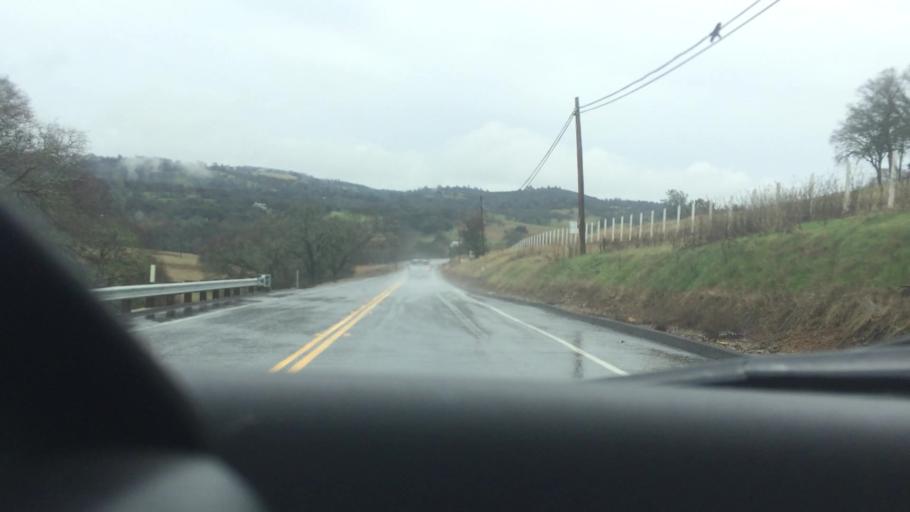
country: US
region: California
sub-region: El Dorado County
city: Cameron Park
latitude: 38.6053
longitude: -121.0296
